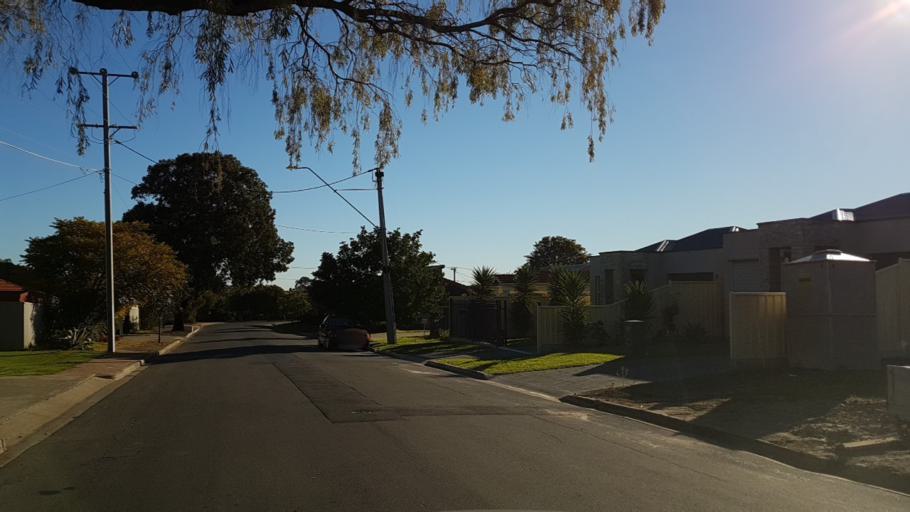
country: AU
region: South Australia
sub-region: Campbelltown
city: Paradise
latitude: -34.8791
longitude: 138.6813
